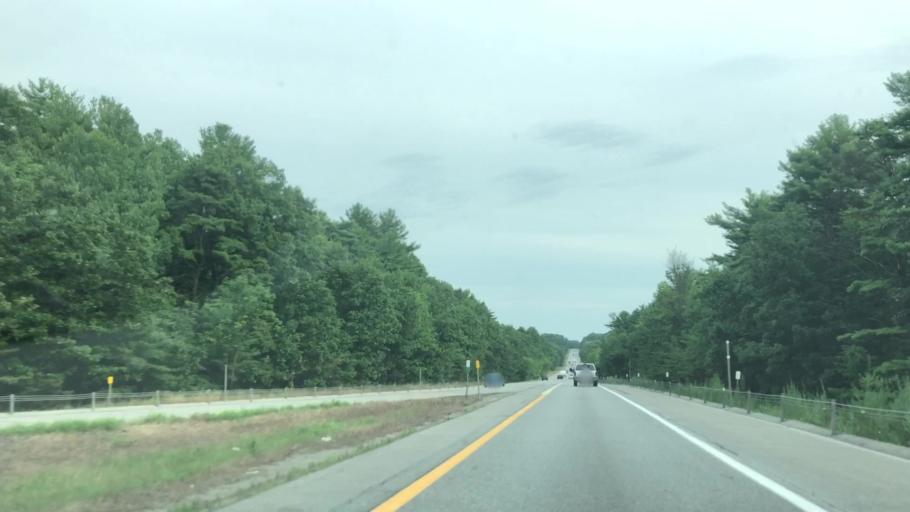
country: US
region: New York
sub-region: Warren County
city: Glens Falls North
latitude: 43.3562
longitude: -73.7037
